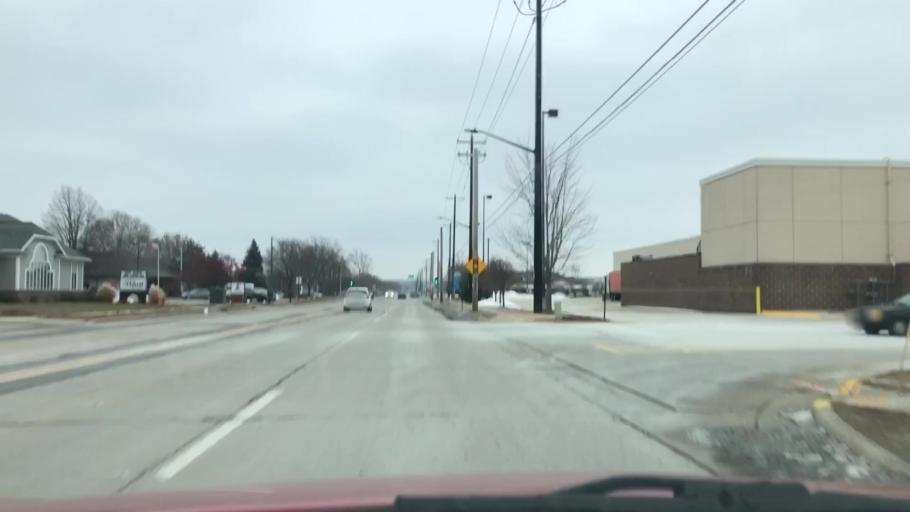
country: US
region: Wisconsin
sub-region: Brown County
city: Ashwaubenon
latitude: 44.4886
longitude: -88.0627
